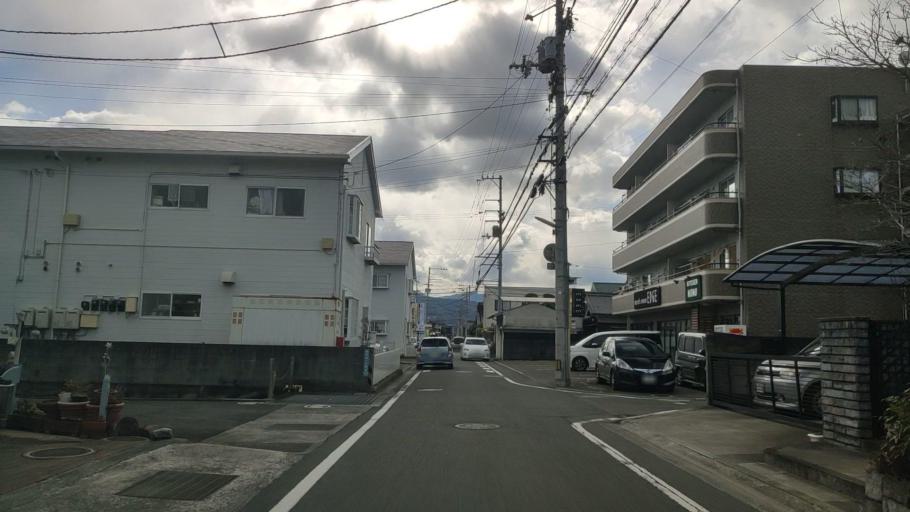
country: JP
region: Ehime
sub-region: Shikoku-chuo Shi
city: Matsuyama
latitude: 33.8127
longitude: 132.7525
